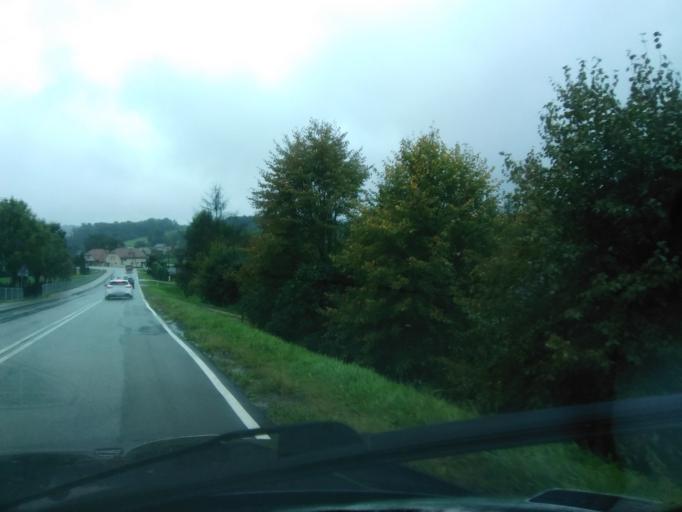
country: PL
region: Subcarpathian Voivodeship
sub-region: Powiat ropczycko-sedziszowski
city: Wielopole Skrzynskie
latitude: 49.9685
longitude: 21.5804
